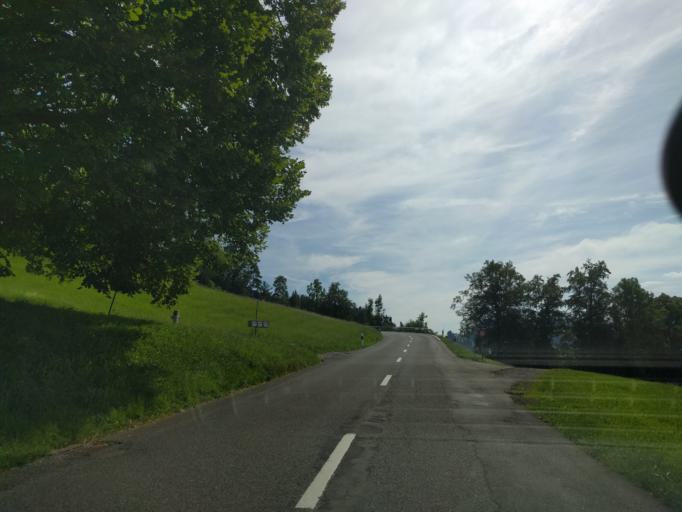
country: CH
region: Saint Gallen
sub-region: Wahlkreis Toggenburg
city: Lichtensteig
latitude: 47.3236
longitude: 9.0959
